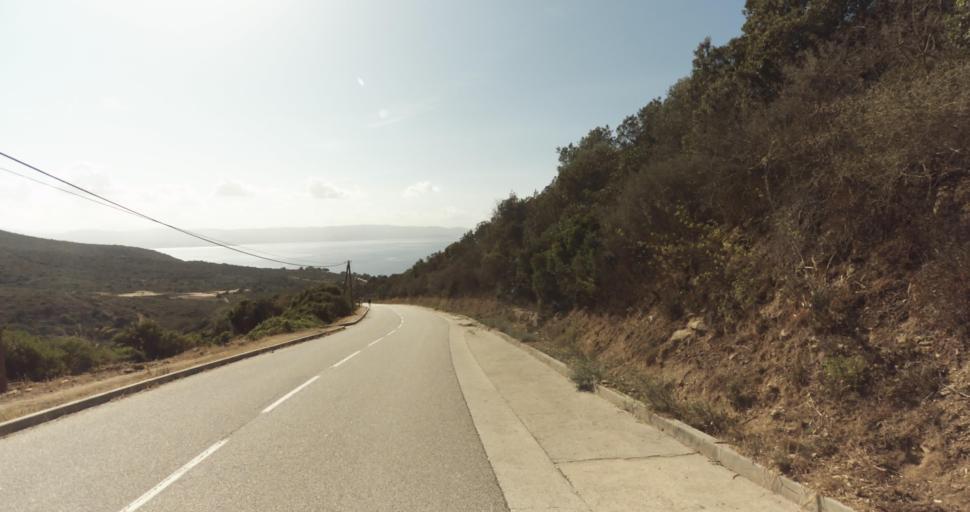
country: FR
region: Corsica
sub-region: Departement de la Corse-du-Sud
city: Ajaccio
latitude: 41.9176
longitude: 8.6415
